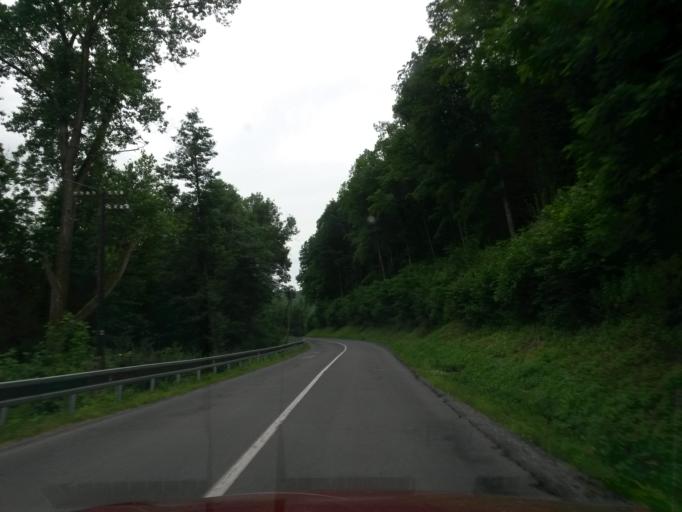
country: SK
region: Banskobystricky
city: Velky Krtis
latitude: 48.3295
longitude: 19.4100
